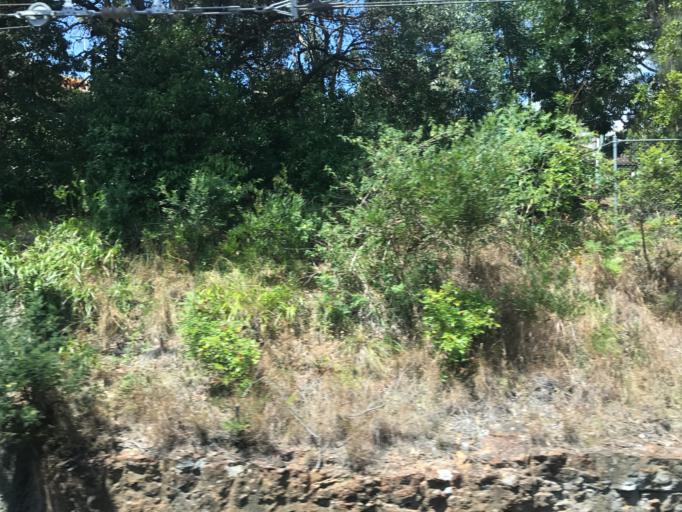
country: AU
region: New South Wales
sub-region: North Sydney
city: St Leonards
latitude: -33.8264
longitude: 151.1954
